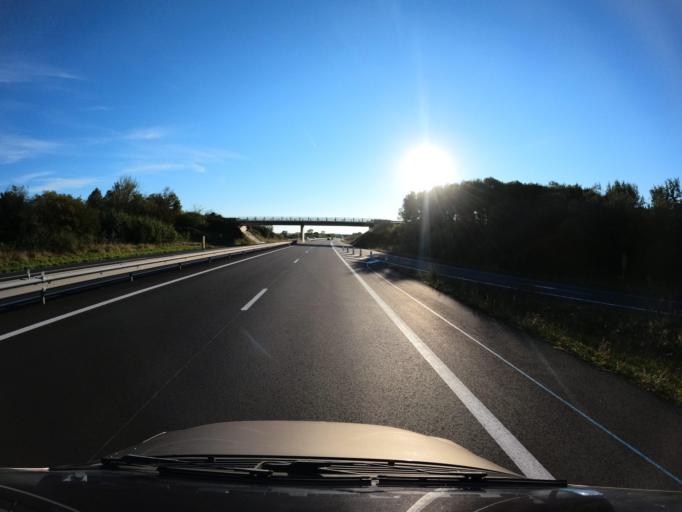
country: FR
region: Pays de la Loire
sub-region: Departement de la Vendee
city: Beaurepaire
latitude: 46.9037
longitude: -1.0540
